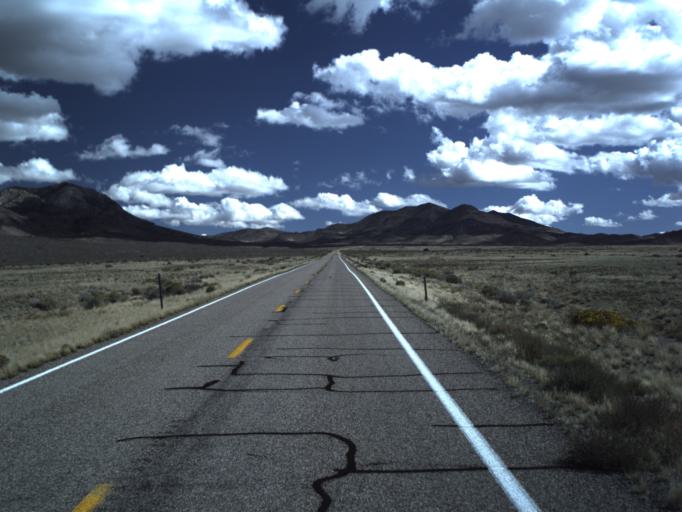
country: US
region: Utah
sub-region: Beaver County
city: Milford
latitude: 38.4525
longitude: -113.3518
